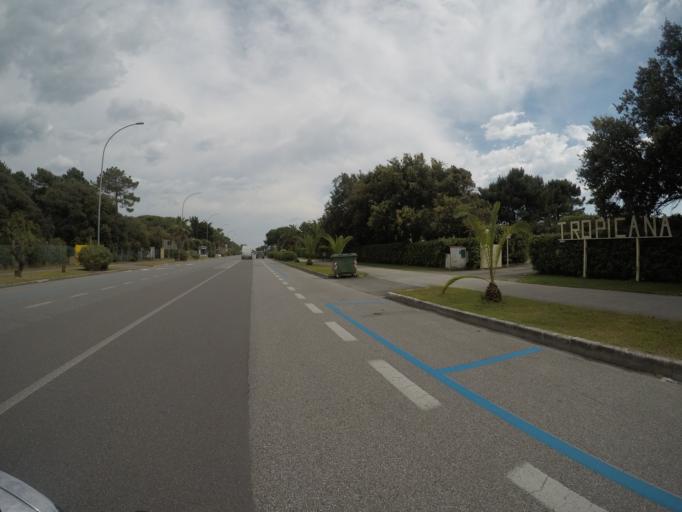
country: IT
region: Tuscany
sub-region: Provincia di Massa-Carrara
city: Capanne-Prato-Cinquale
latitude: 43.9873
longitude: 10.1306
